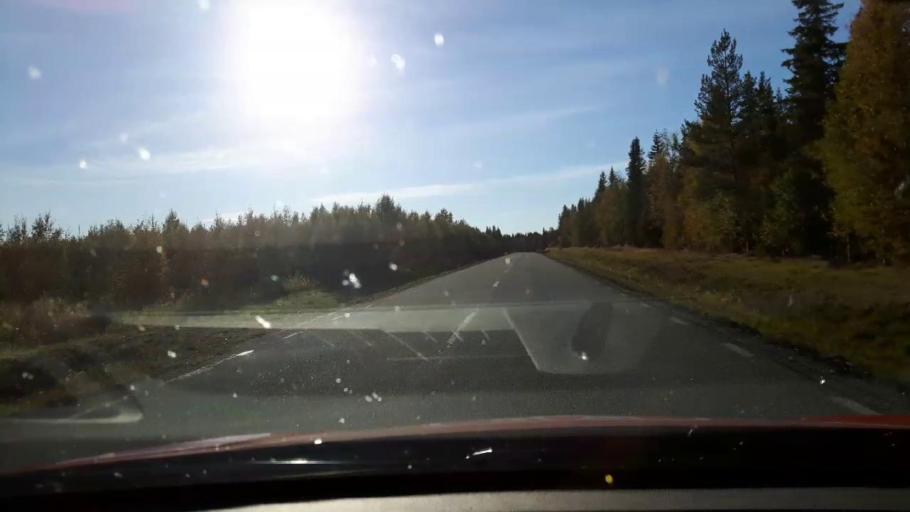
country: SE
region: Jaemtland
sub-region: Stroemsunds Kommun
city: Stroemsund
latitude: 63.8613
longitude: 15.0431
